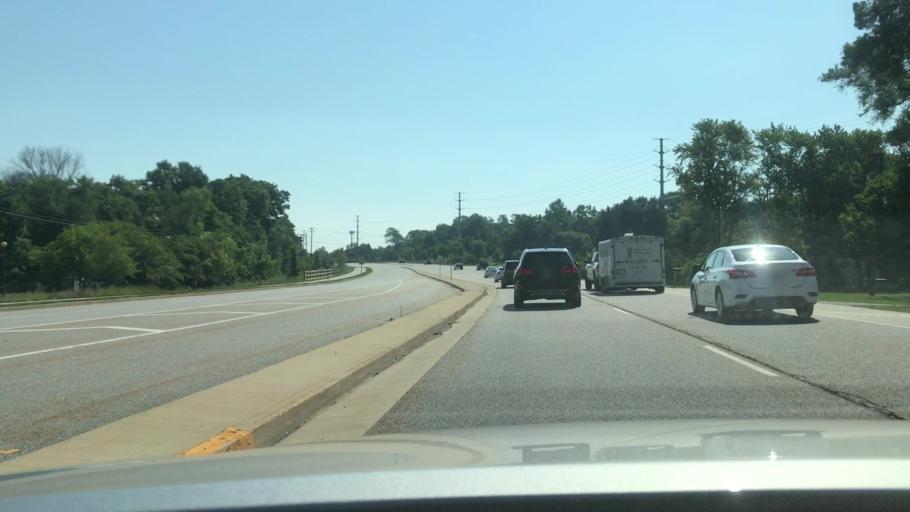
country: US
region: Illinois
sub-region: DuPage County
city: Warrenville
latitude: 41.8202
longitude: -88.1944
